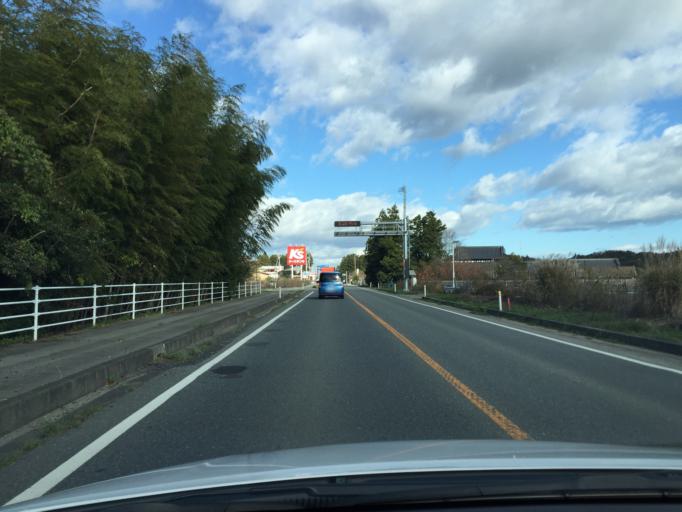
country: JP
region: Fukushima
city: Namie
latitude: 37.3628
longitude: 141.0096
